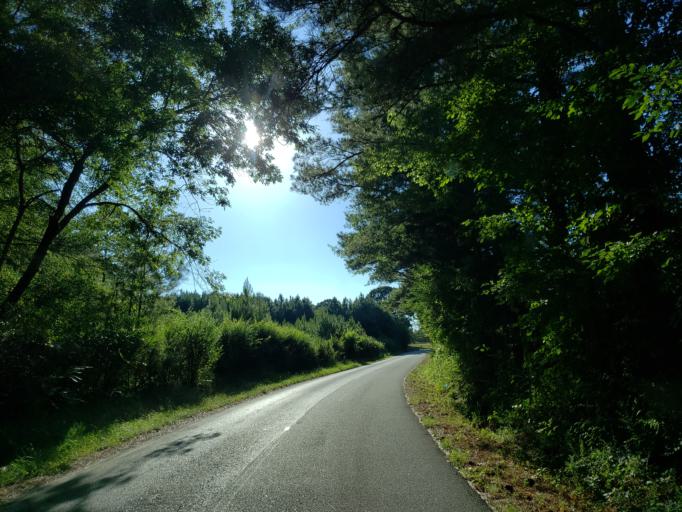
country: US
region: Georgia
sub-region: Bartow County
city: Euharlee
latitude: 34.1189
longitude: -84.9983
